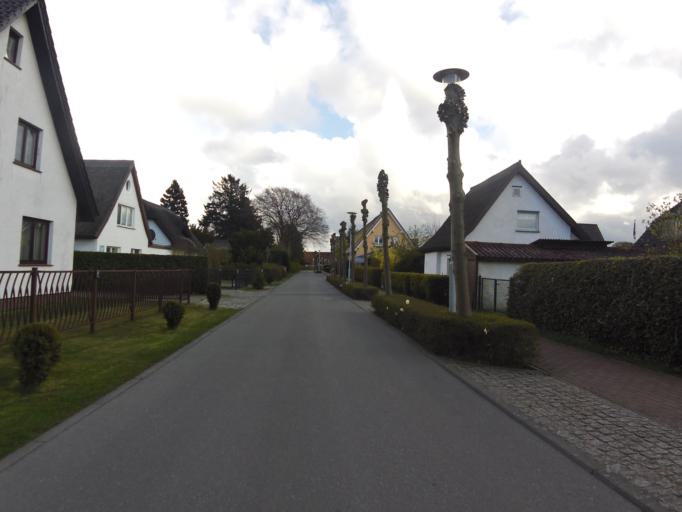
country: DE
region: Mecklenburg-Vorpommern
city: Zingst
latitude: 54.4403
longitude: 12.6901
